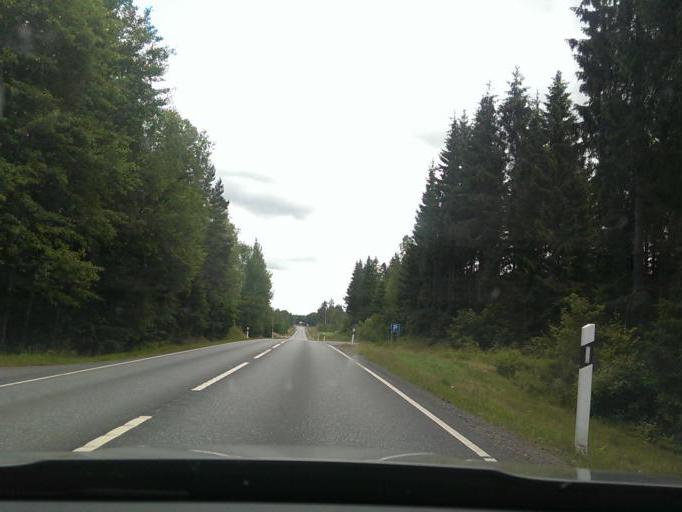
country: SE
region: Joenkoeping
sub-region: Varnamo Kommun
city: Varnamo
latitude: 57.2153
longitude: 14.0182
